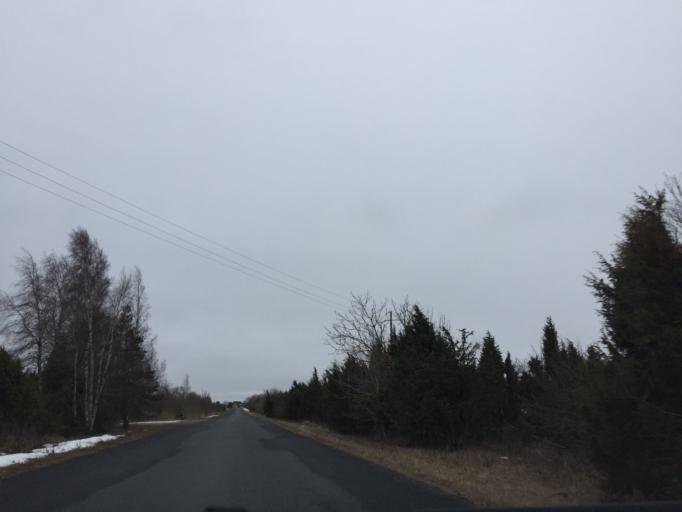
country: EE
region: Laeaene
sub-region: Haapsalu linn
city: Haapsalu
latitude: 58.7721
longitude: 23.4581
